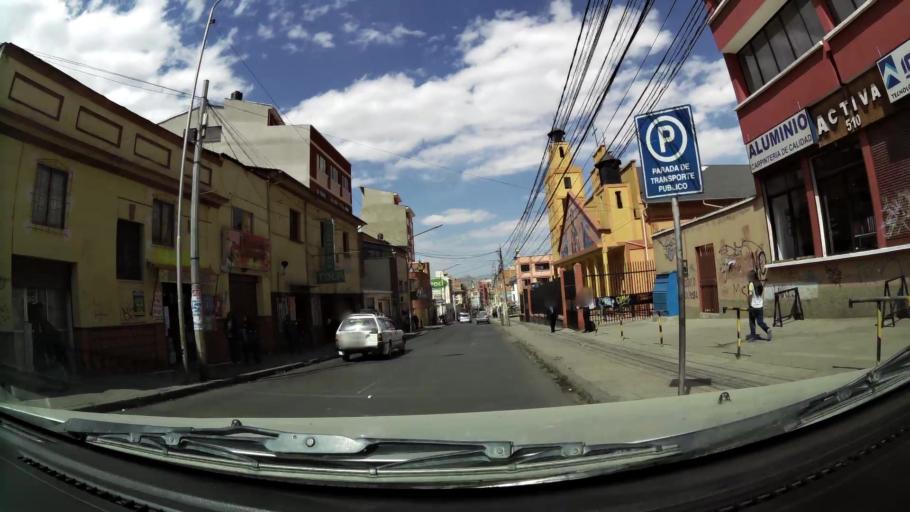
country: BO
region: La Paz
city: La Paz
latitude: -16.4900
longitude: -68.1381
